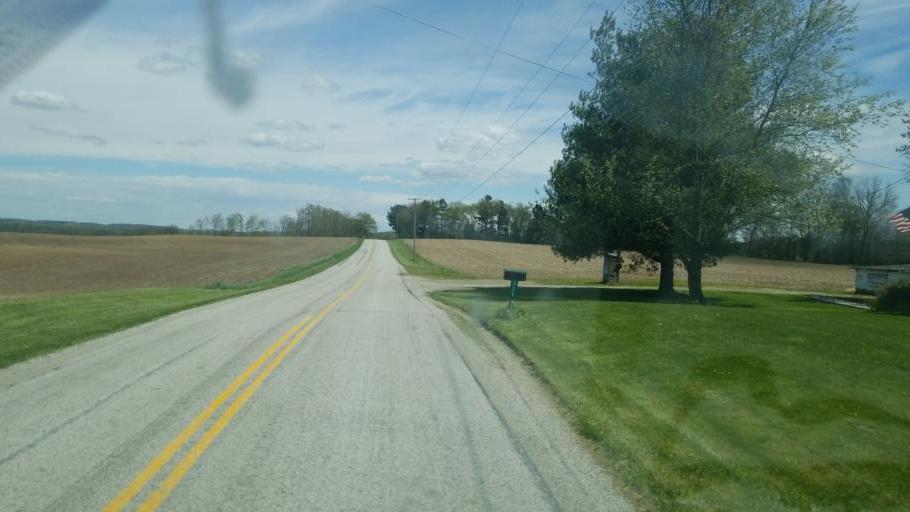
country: US
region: Ohio
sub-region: Ashland County
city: Loudonville
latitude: 40.7662
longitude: -82.1659
